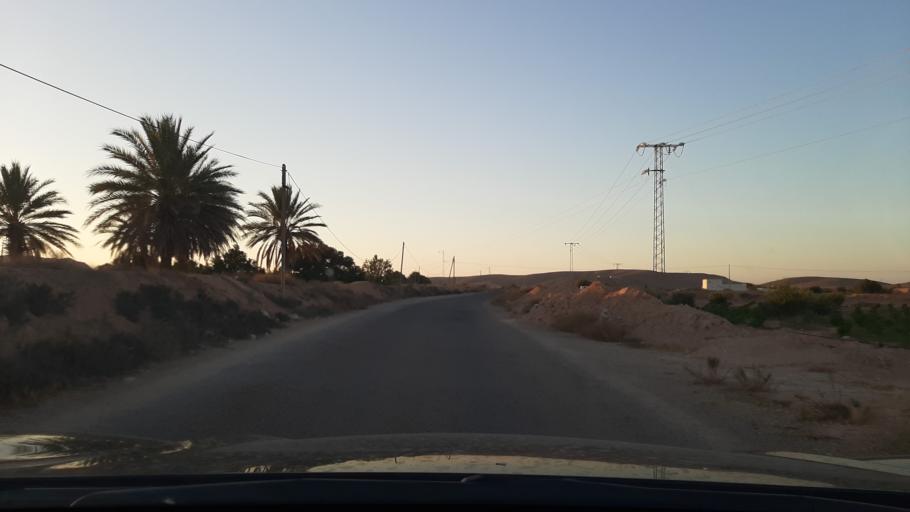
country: TN
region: Qabis
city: Matmata
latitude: 33.5583
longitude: 10.1837
